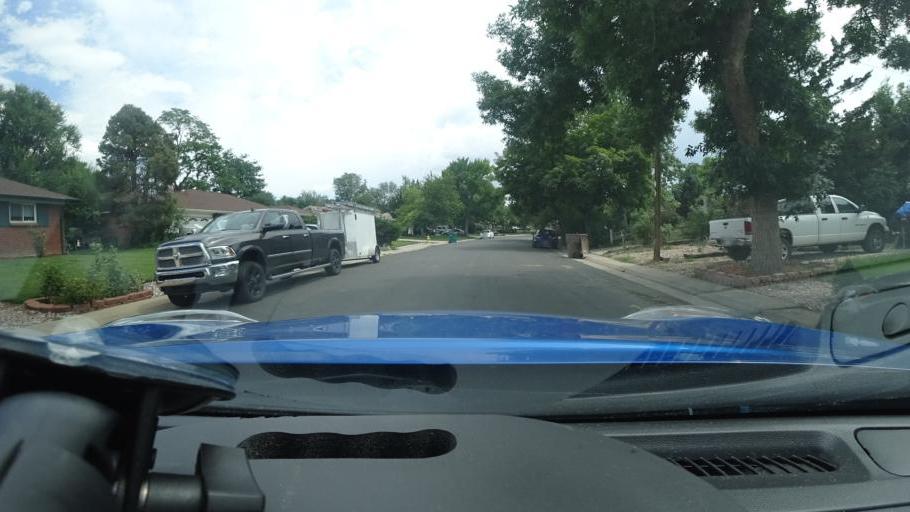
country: US
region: Colorado
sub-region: Adams County
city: Aurora
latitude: 39.7240
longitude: -104.8340
